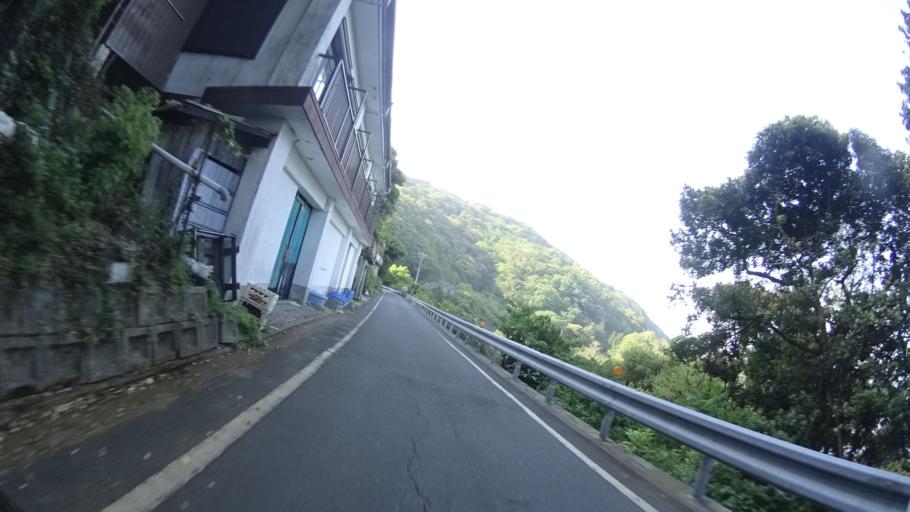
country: JP
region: Oita
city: Tsukumiura
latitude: 33.3563
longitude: 132.0314
